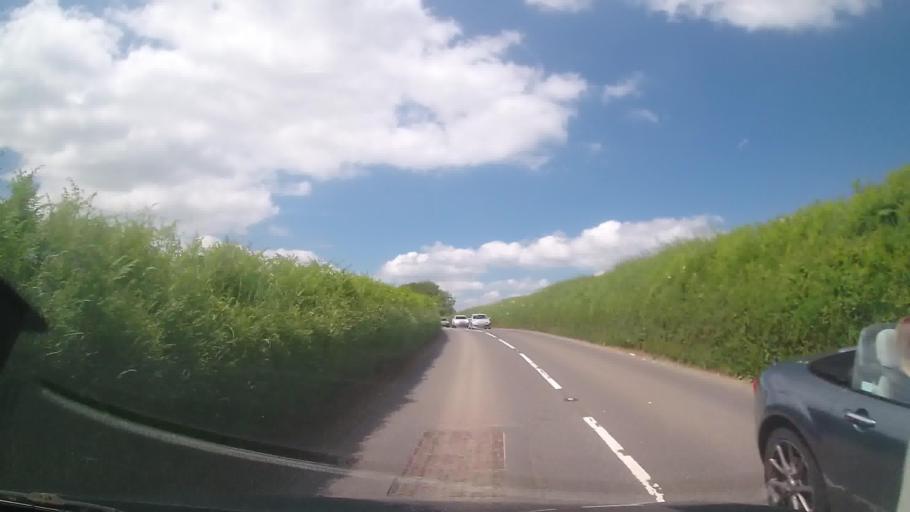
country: GB
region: England
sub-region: Devon
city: Dartmouth
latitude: 50.3524
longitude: -3.6259
